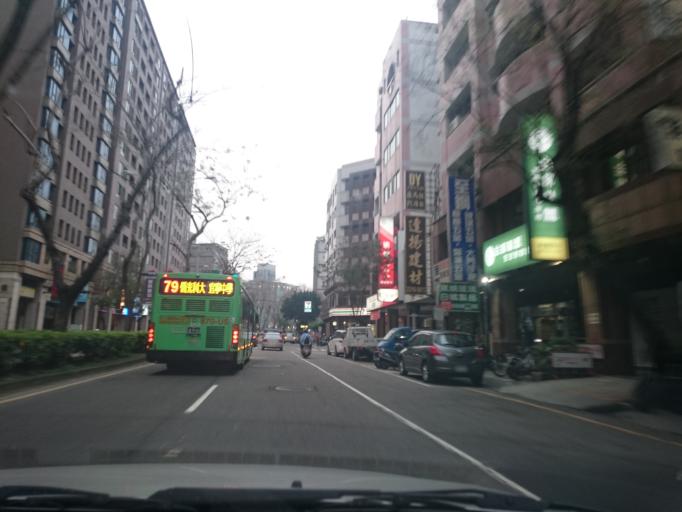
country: TW
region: Taiwan
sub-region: Taichung City
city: Taichung
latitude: 24.1521
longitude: 120.6573
